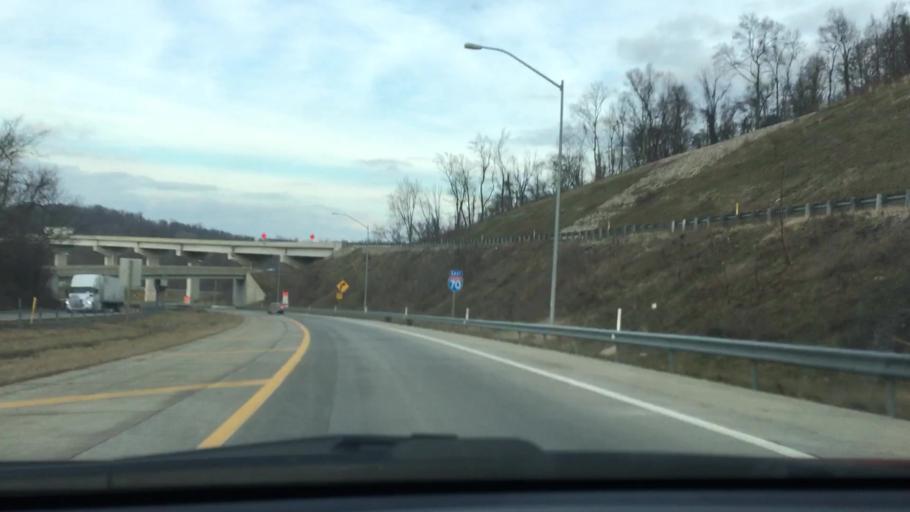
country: US
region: Pennsylvania
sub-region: Washington County
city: East Washington
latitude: 40.1587
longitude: -80.1944
